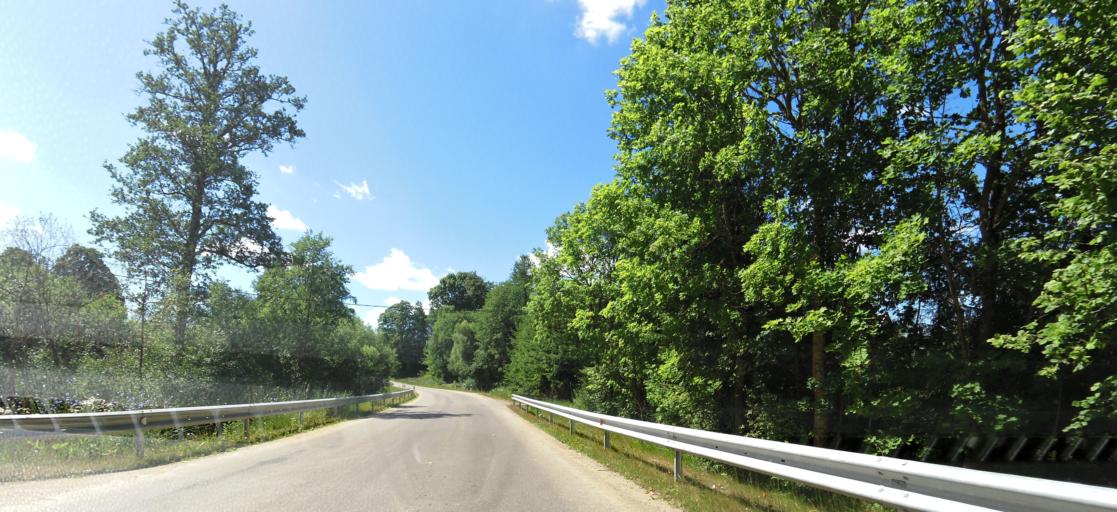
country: LT
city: Kupiskis
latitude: 55.9537
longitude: 24.9827
